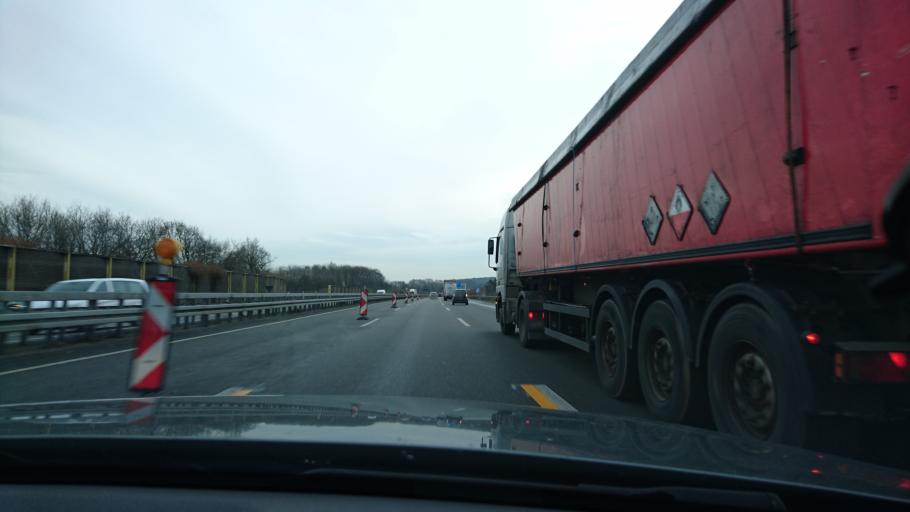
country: DE
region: North Rhine-Westphalia
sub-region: Regierungsbezirk Munster
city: Lotte
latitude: 52.3000
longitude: 7.9429
